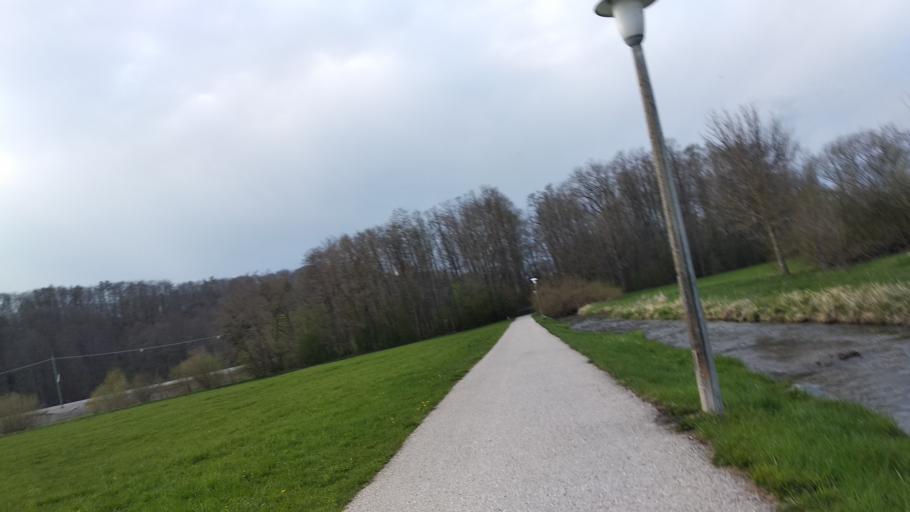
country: DE
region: Bavaria
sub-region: Swabia
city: Mindelheim
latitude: 48.0312
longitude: 10.4912
